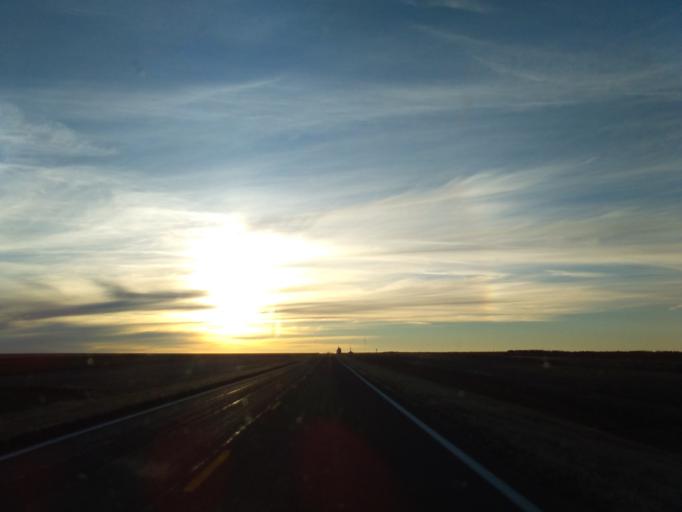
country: US
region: Kansas
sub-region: Logan County
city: Oakley
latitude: 39.0733
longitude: -101.2067
